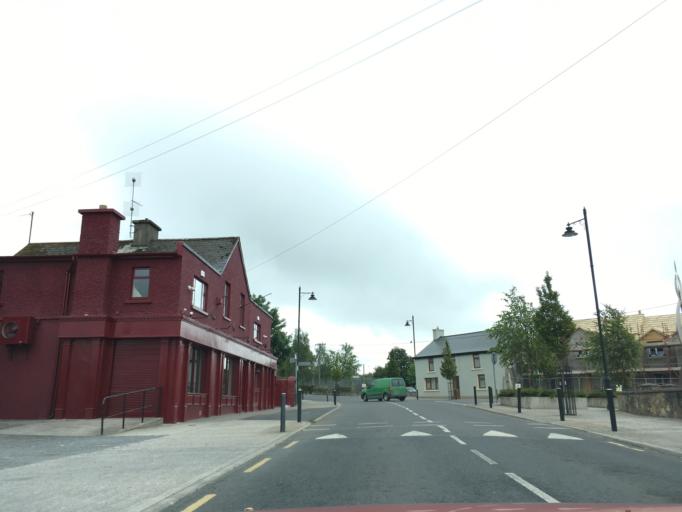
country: IE
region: Munster
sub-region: South Tipperary
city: Cluain Meala
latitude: 52.4126
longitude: -7.7557
